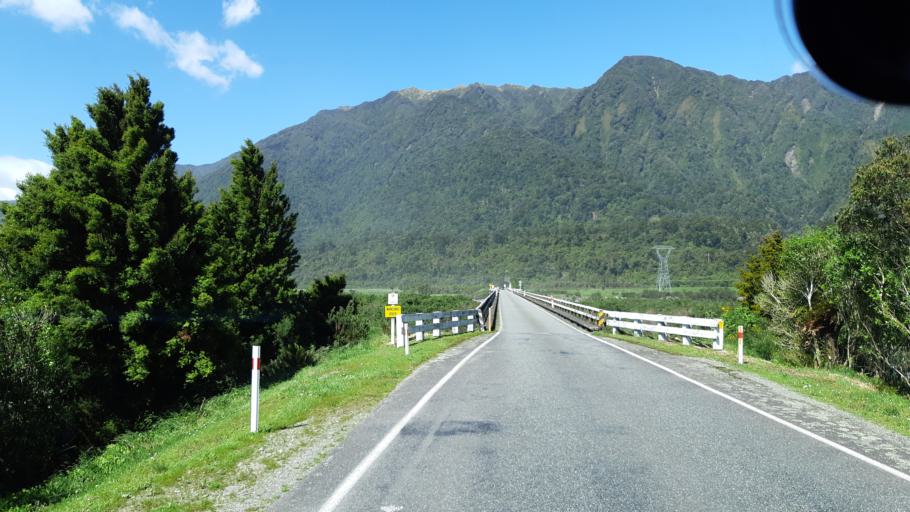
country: NZ
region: West Coast
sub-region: Westland District
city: Hokitika
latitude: -43.1555
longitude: 170.6207
